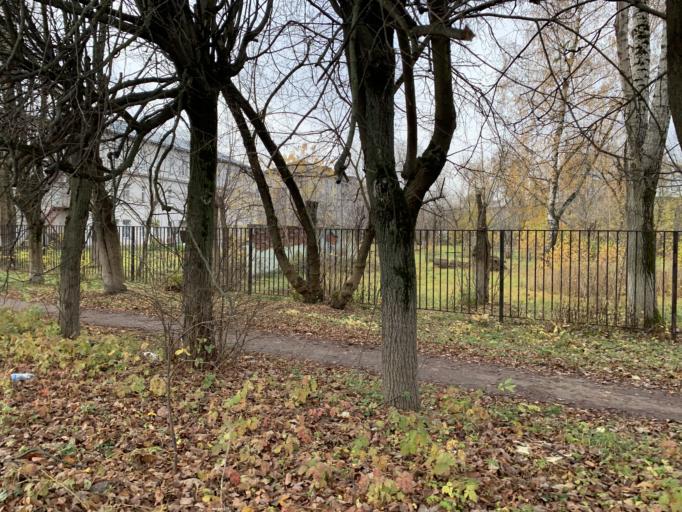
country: RU
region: Moskovskaya
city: Lesnyye Polyany
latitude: 55.9885
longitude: 37.8502
